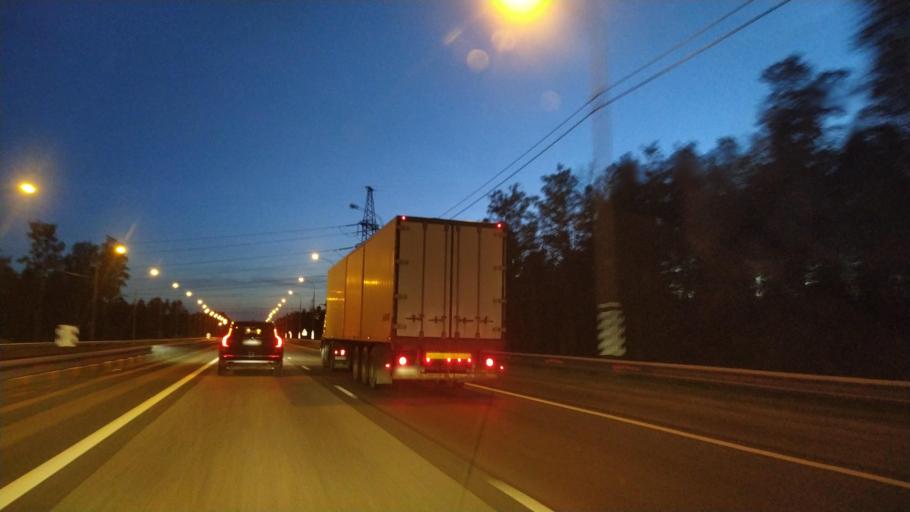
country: RU
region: Leningrad
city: Yanino Vtoroye
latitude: 59.8905
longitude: 30.5660
